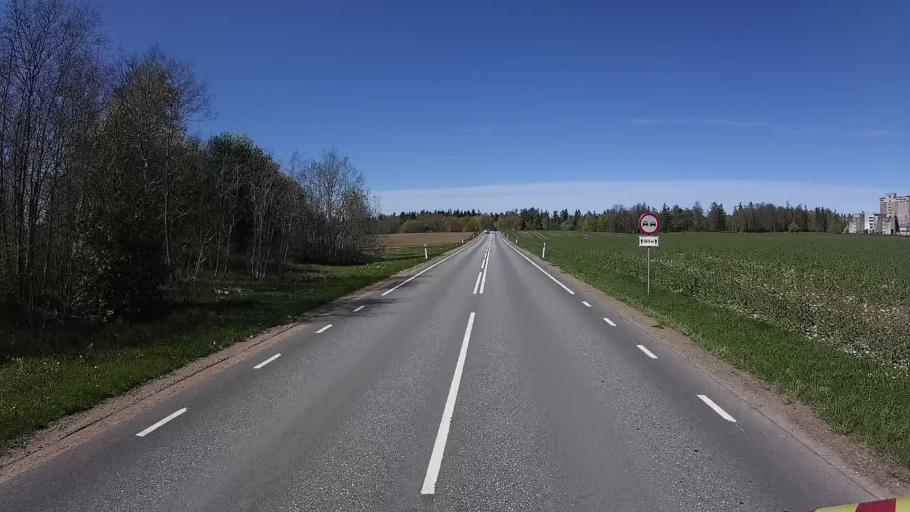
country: EE
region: Laeaene-Virumaa
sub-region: Tapa vald
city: Tapa
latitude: 59.3514
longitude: 26.0030
